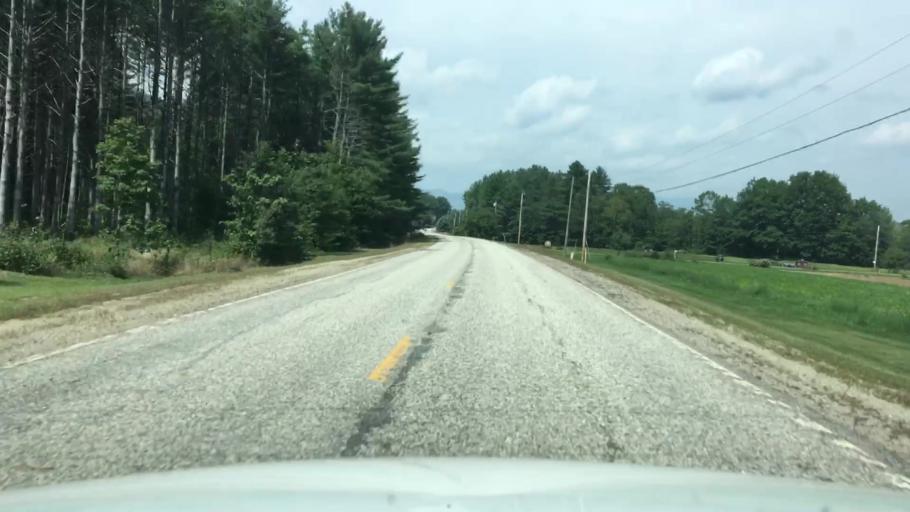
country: US
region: Maine
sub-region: Oxford County
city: Rumford
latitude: 44.5851
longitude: -70.7344
